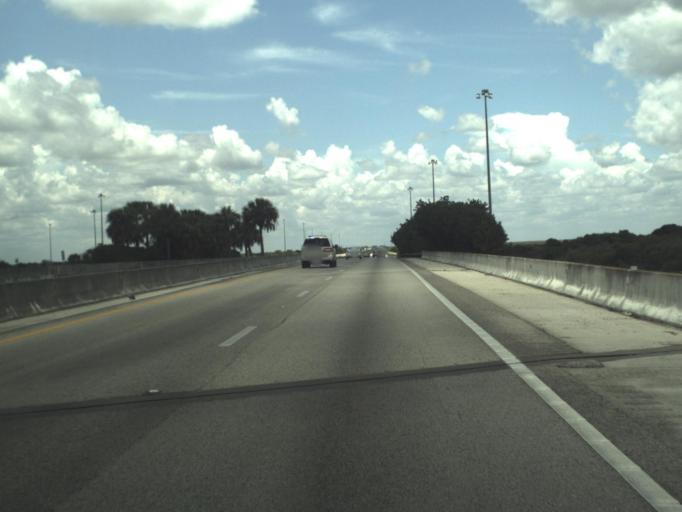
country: US
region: Florida
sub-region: Broward County
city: Weston
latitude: 26.1466
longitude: -80.6328
